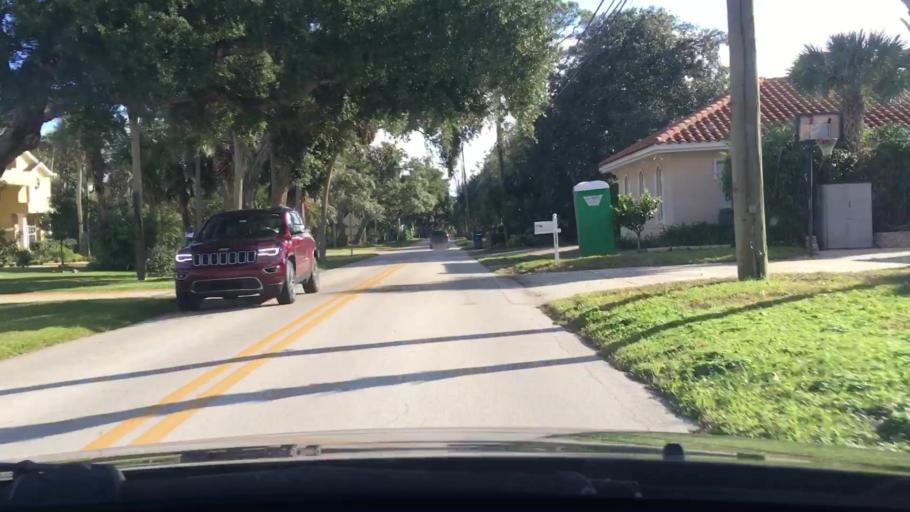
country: US
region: Florida
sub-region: Volusia County
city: Ormond-by-the-Sea
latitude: 29.3463
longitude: -81.0726
